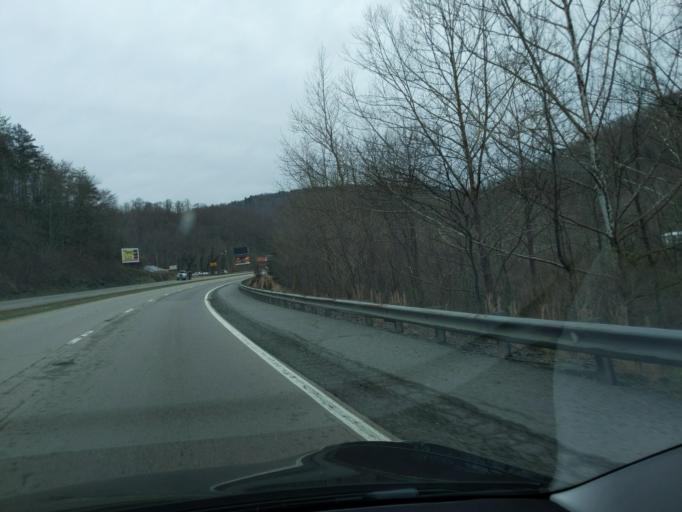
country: US
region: Kentucky
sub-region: Bell County
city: Middlesboro
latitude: 36.6627
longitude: -83.6957
